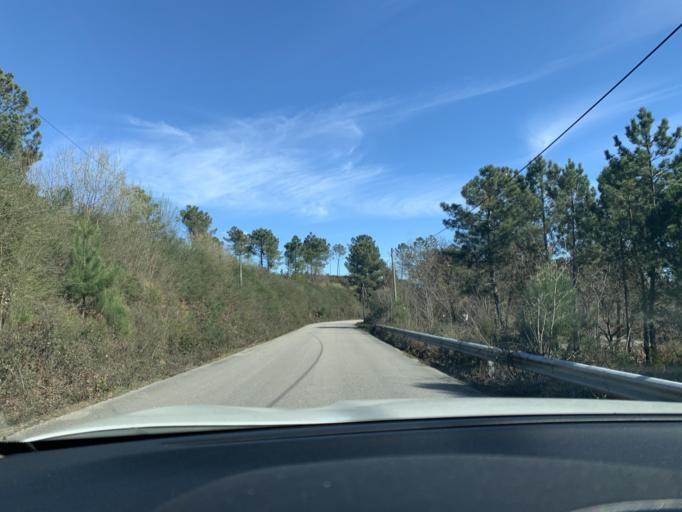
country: PT
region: Viseu
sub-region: Concelho de Tondela
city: Tondela
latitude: 40.6056
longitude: -8.0338
